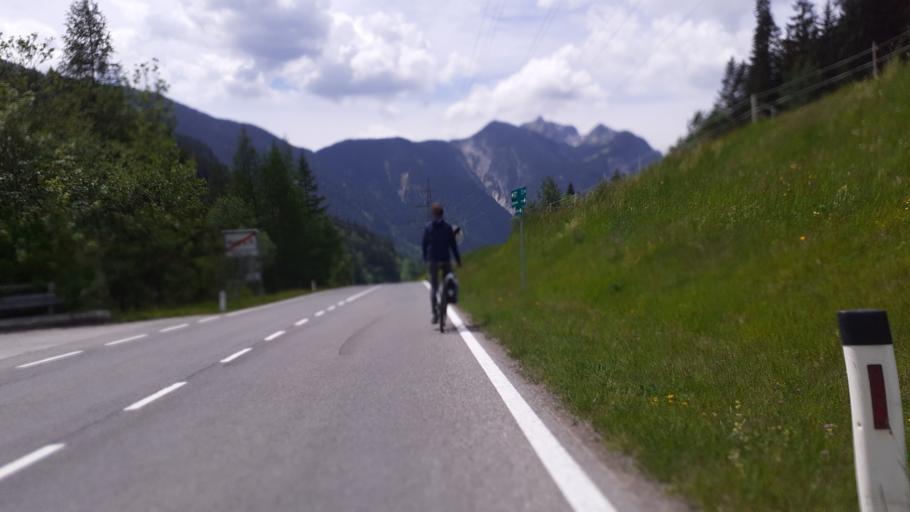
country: AT
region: Vorarlberg
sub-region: Politischer Bezirk Bludenz
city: Dalaas
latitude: 47.1276
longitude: 10.0285
